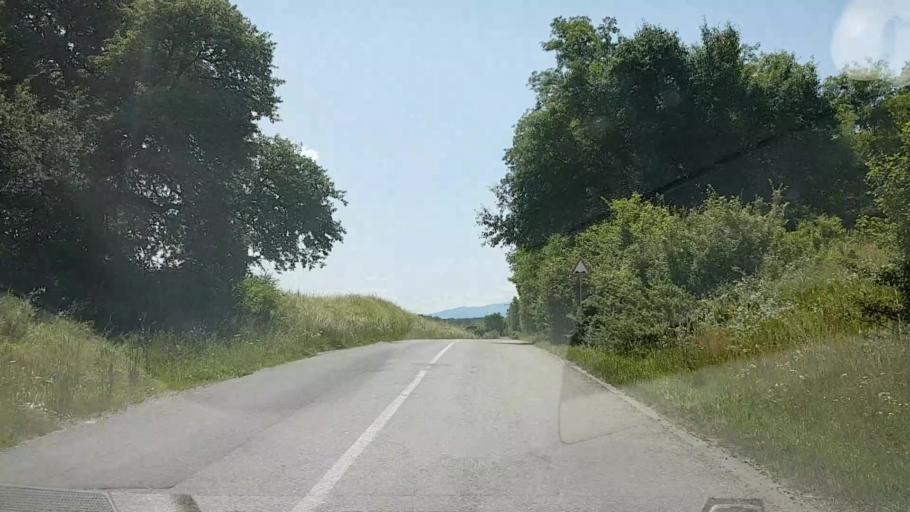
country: RO
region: Brasov
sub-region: Comuna Cincu
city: Cincu
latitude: 45.8693
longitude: 24.8226
